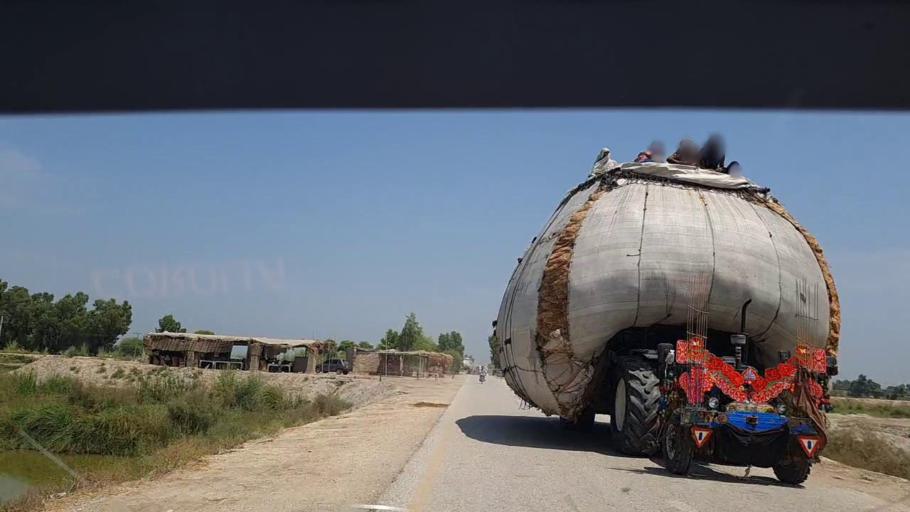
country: PK
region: Sindh
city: Thul
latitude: 28.1158
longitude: 68.8111
